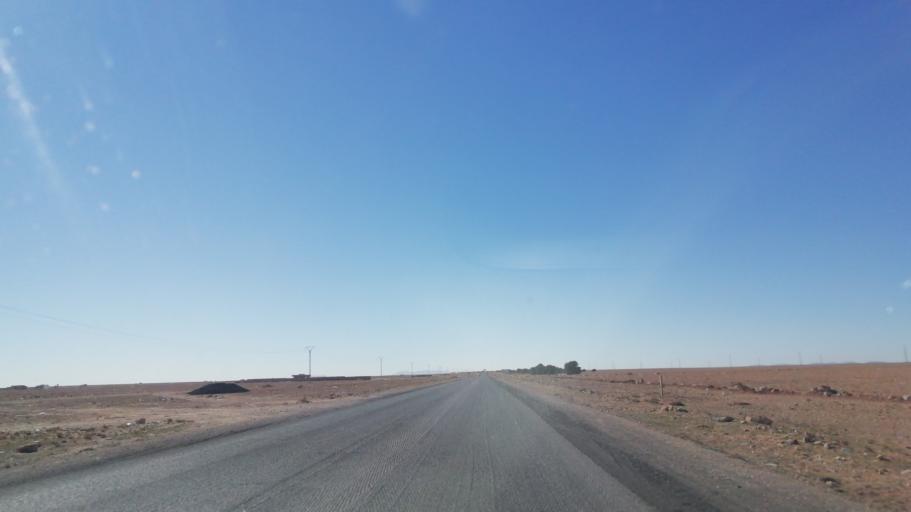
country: DZ
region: Saida
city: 'Ain el Hadjar
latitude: 34.0189
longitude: 0.0621
